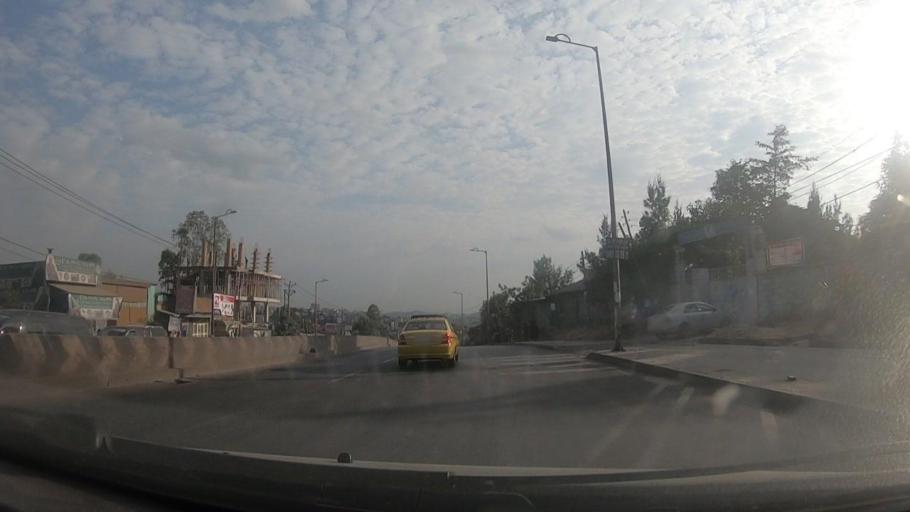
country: ET
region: Adis Abeba
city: Addis Ababa
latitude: 8.9784
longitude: 38.7339
